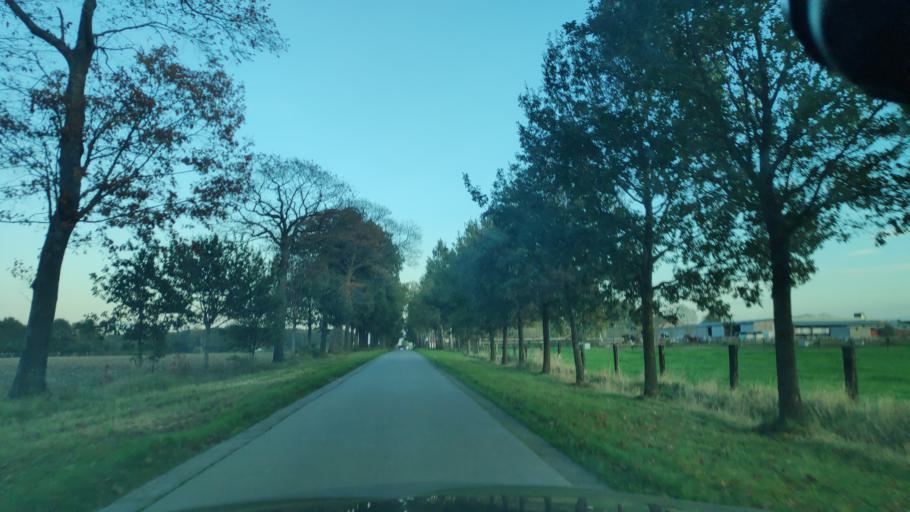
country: BE
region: Flanders
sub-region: Provincie Oost-Vlaanderen
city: Maldegem
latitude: 51.1590
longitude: 3.4786
